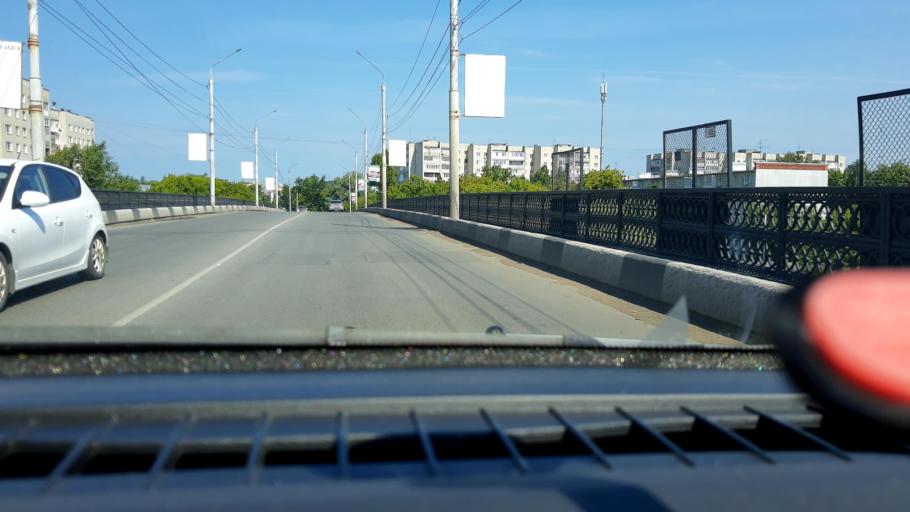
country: RU
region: Nizjnij Novgorod
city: Dzerzhinsk
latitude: 56.2347
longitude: 43.4892
